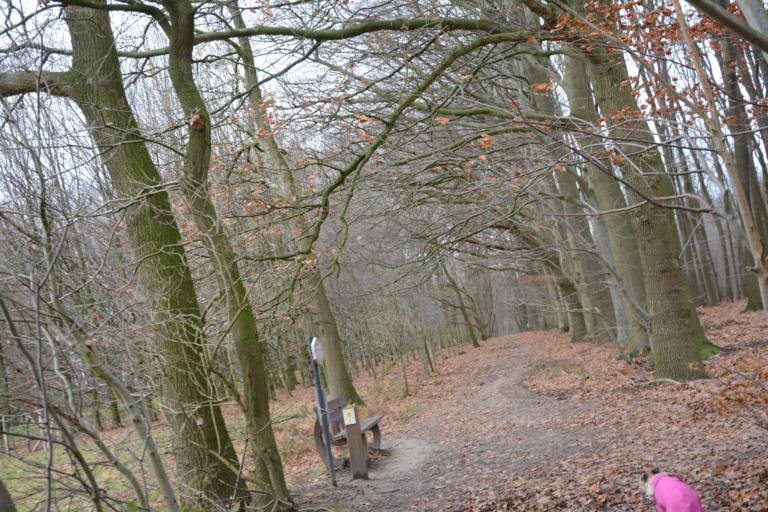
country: BE
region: Flanders
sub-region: Provincie Vlaams-Brabant
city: Opwijk
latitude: 50.9362
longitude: 4.1572
